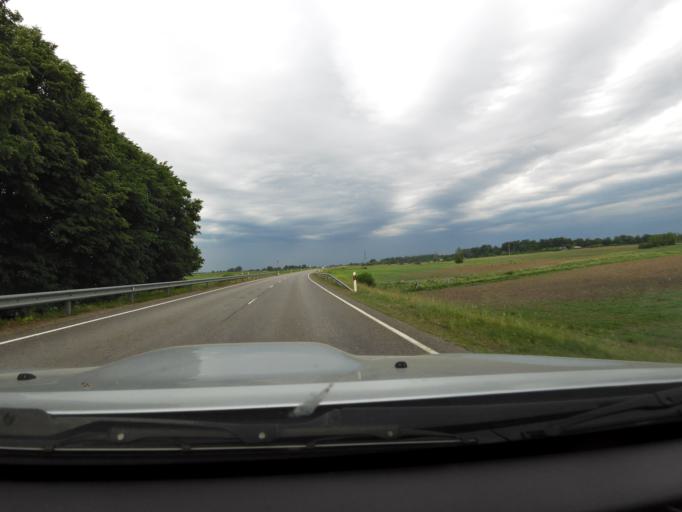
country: LT
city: Jieznas
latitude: 54.5778
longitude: 24.2828
